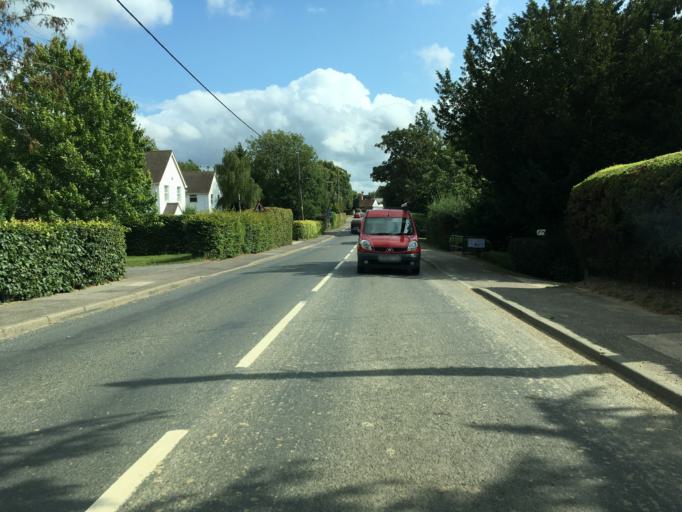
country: GB
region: England
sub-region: Kent
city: Headcorn
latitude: 51.1703
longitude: 0.6191
